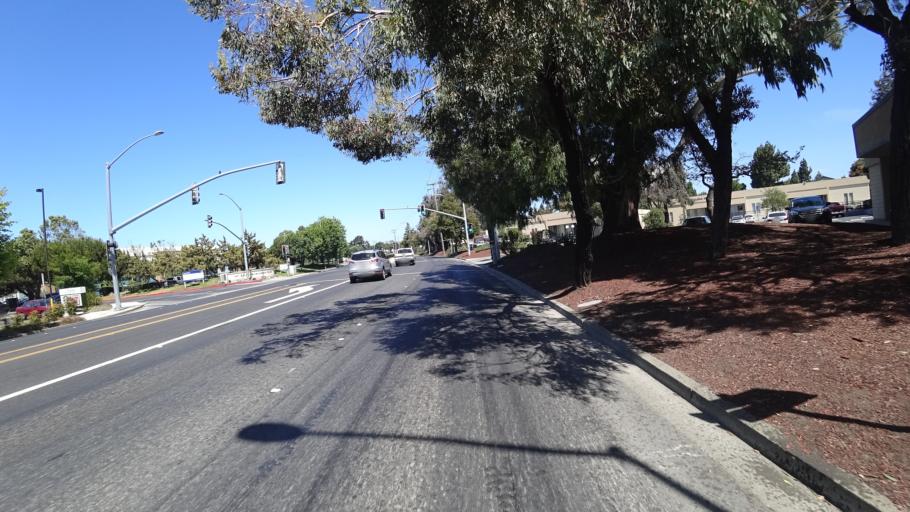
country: US
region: California
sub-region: Alameda County
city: Cherryland
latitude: 37.6339
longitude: -122.1112
